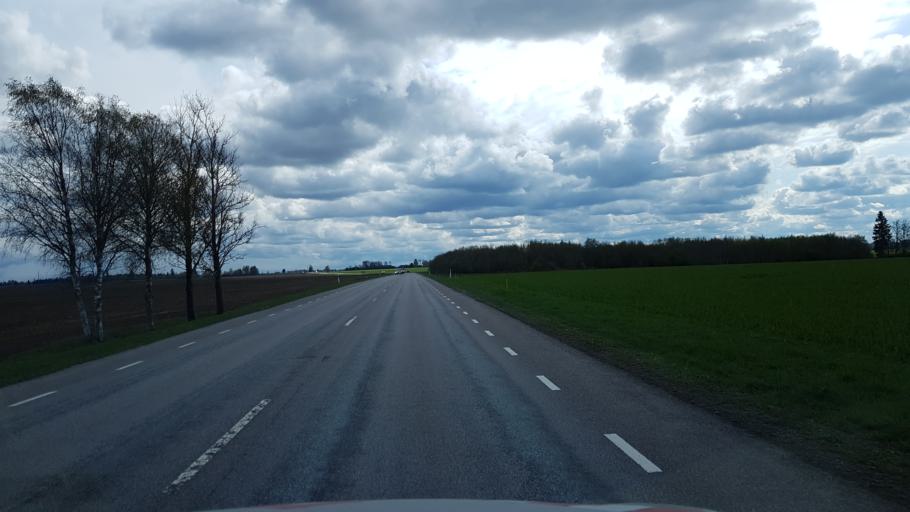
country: EE
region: Laeaene-Virumaa
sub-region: Vaeike-Maarja vald
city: Vaike-Maarja
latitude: 59.1949
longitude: 26.2664
